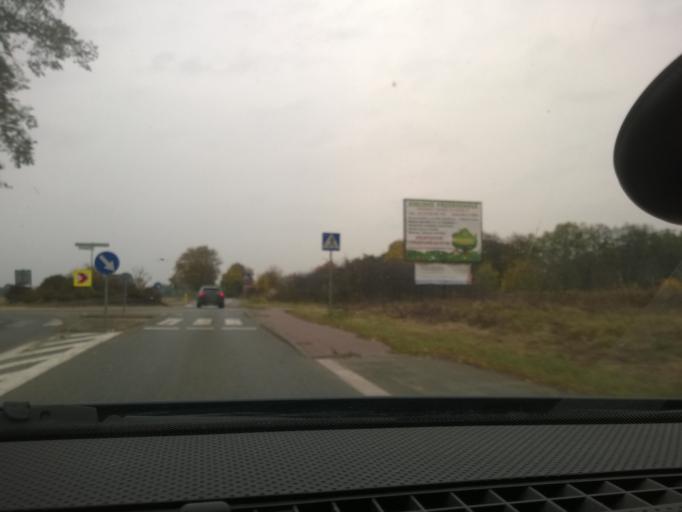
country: PL
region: Masovian Voivodeship
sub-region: Powiat pruszkowski
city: Komorow
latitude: 52.1566
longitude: 20.8354
